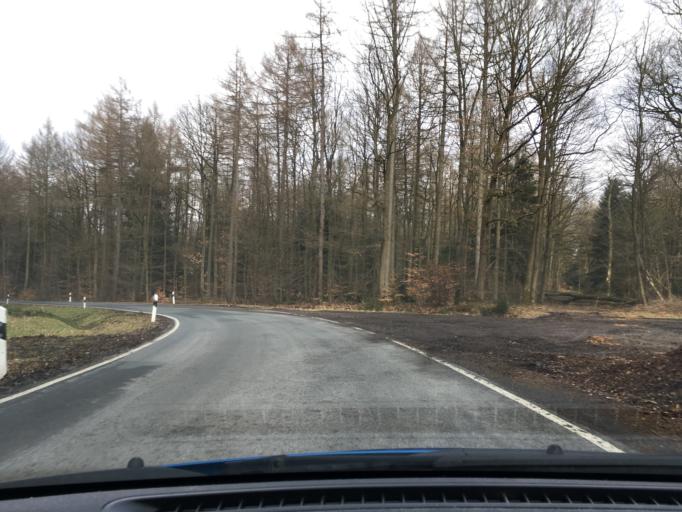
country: DE
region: Lower Saxony
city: Buhren
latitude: 51.5001
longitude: 9.6572
